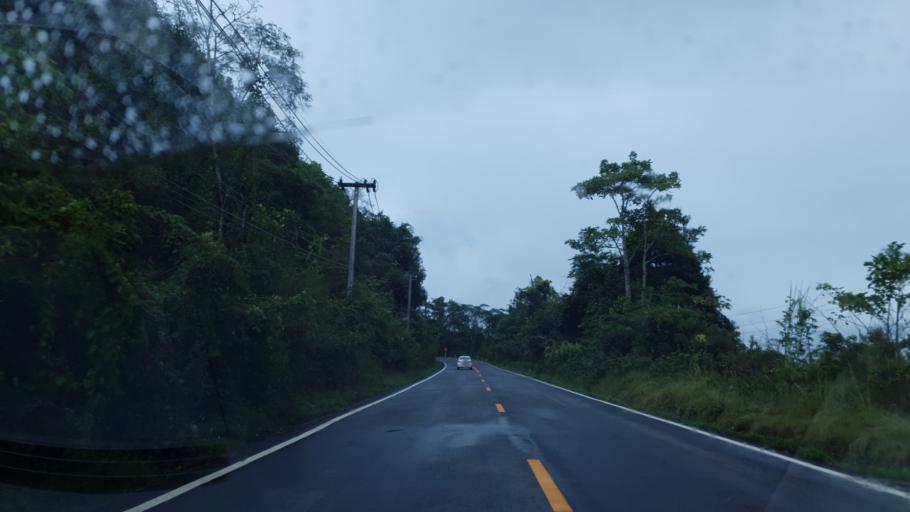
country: TH
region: Mae Hong Son
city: Ban Huai I Huak
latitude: 18.1441
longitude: 98.1206
